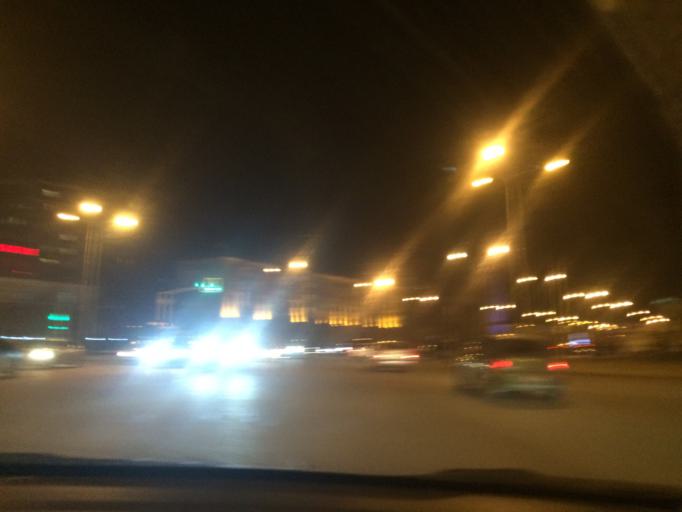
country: KZ
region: Astana Qalasy
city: Astana
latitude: 51.1912
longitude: 71.4068
